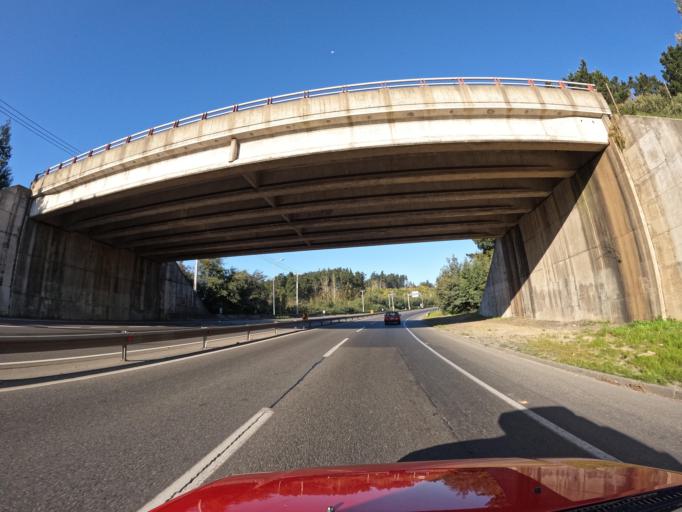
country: CL
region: Biobio
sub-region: Provincia de Concepcion
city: Penco
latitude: -36.7506
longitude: -72.9897
